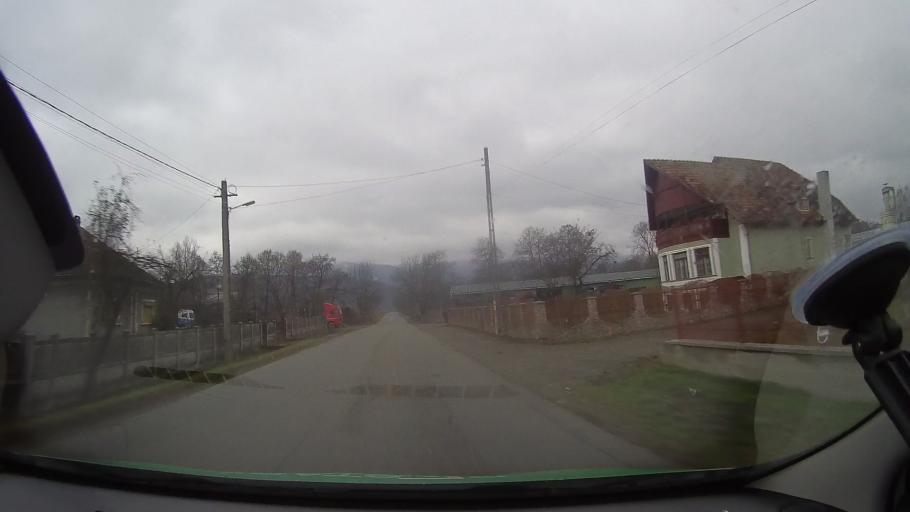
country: RO
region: Hunedoara
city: Vata de Jos
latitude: 46.1880
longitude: 22.6066
